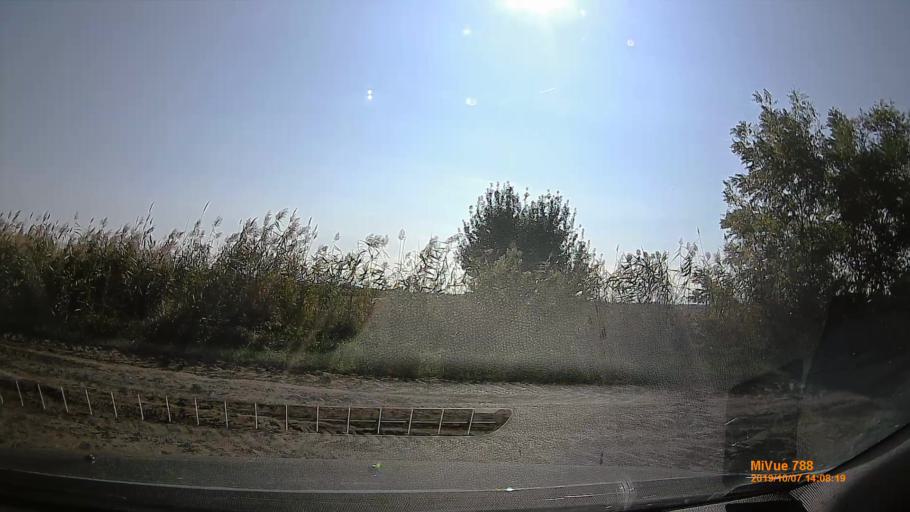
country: HU
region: Jasz-Nagykun-Szolnok
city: Cserkeszolo
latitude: 46.8697
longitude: 20.2239
